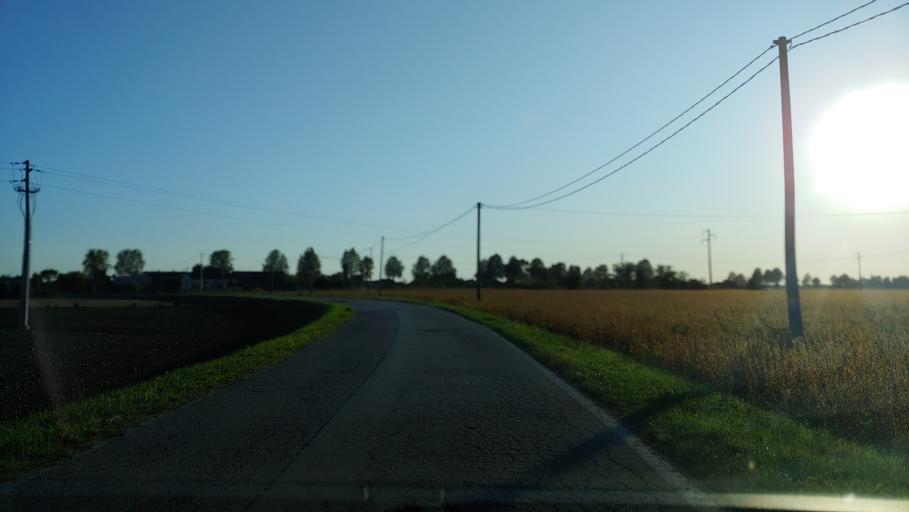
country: IT
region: Veneto
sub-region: Provincia di Rovigo
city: Pettorazza Grimani
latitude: 45.0673
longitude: 11.9846
